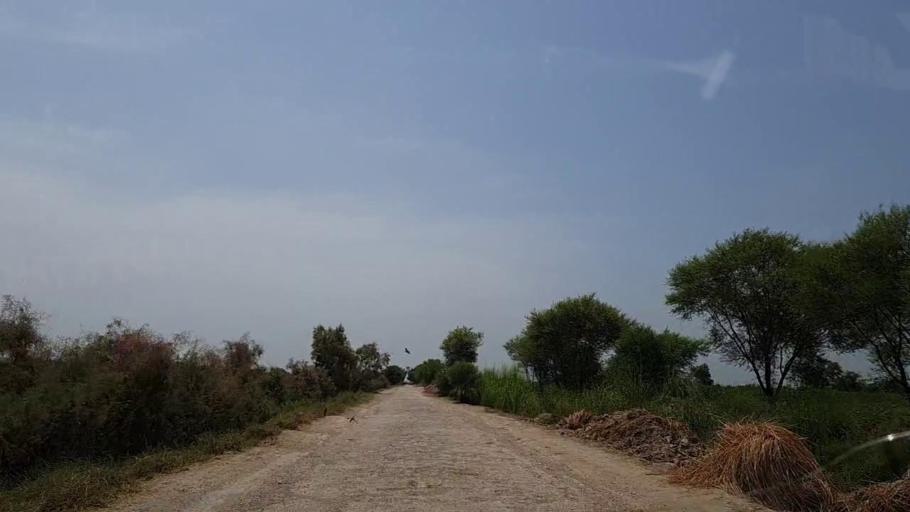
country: PK
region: Sindh
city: Khanpur
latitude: 27.8866
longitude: 69.4941
